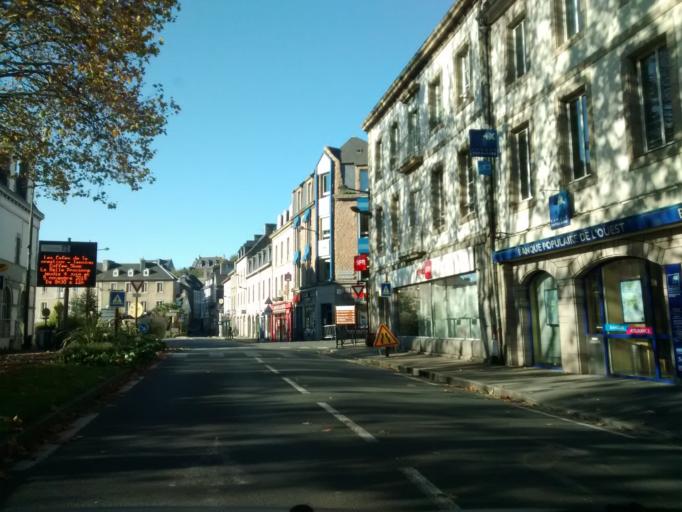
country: FR
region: Brittany
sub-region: Departement des Cotes-d'Armor
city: Lannion
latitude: 48.7321
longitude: -3.4615
